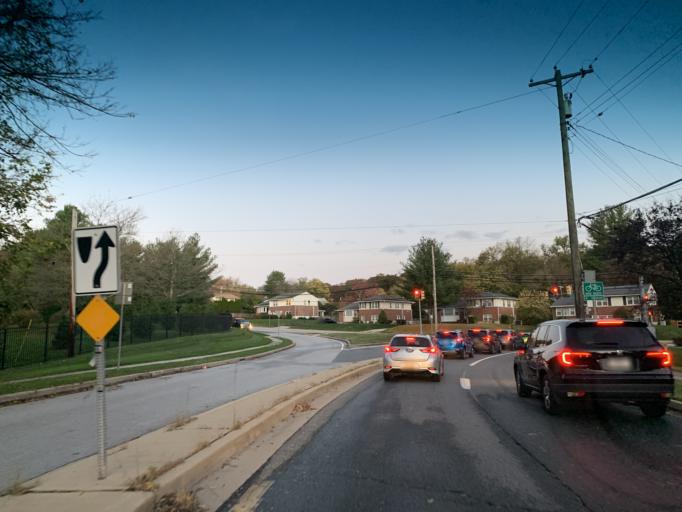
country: US
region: Maryland
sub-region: Baltimore County
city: Towson
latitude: 39.4020
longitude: -76.5847
